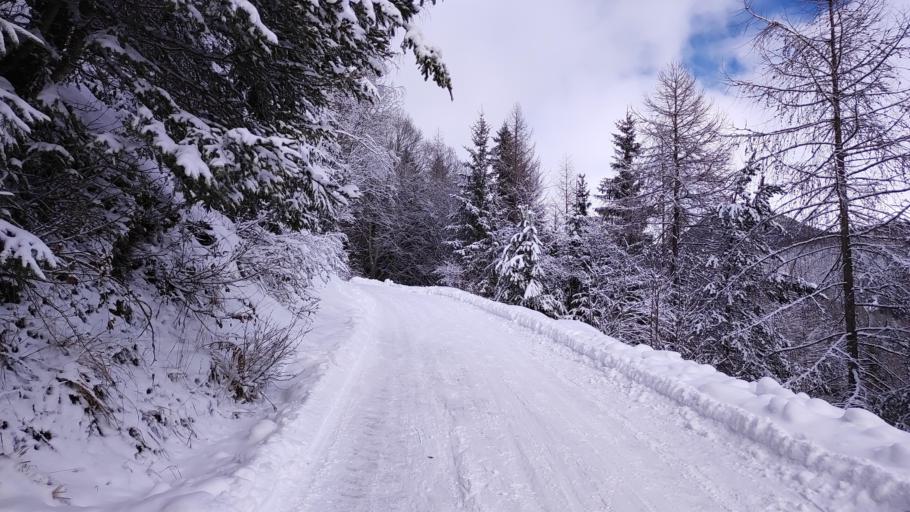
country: AT
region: Tyrol
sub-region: Politischer Bezirk Imst
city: Umhausen
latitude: 47.0999
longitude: 10.9363
